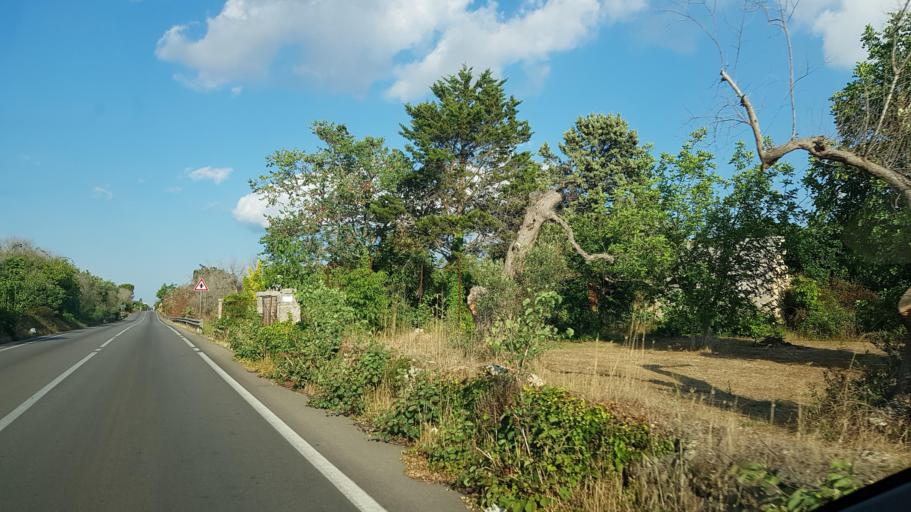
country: IT
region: Apulia
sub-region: Provincia di Lecce
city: Miggiano
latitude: 39.9640
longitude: 18.2926
